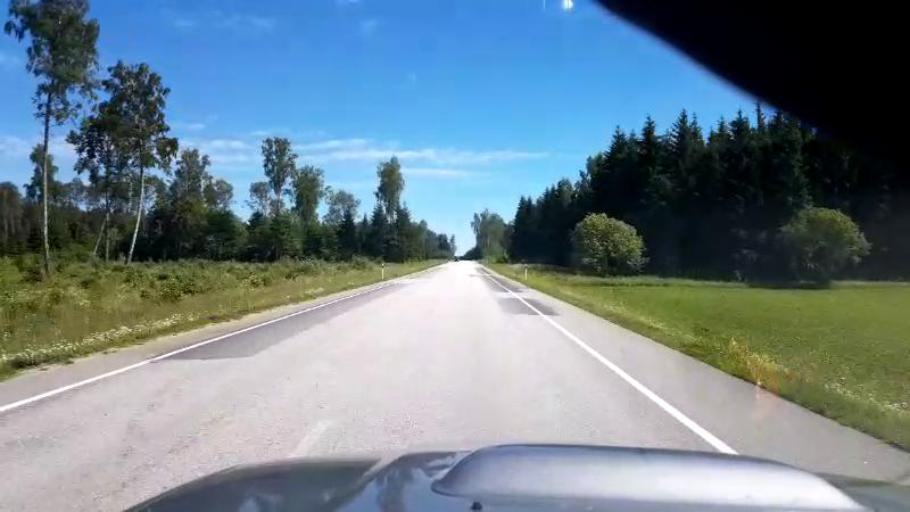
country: EE
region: Jaervamaa
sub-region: Jaerva-Jaani vald
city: Jarva-Jaani
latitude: 58.9948
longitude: 25.9533
